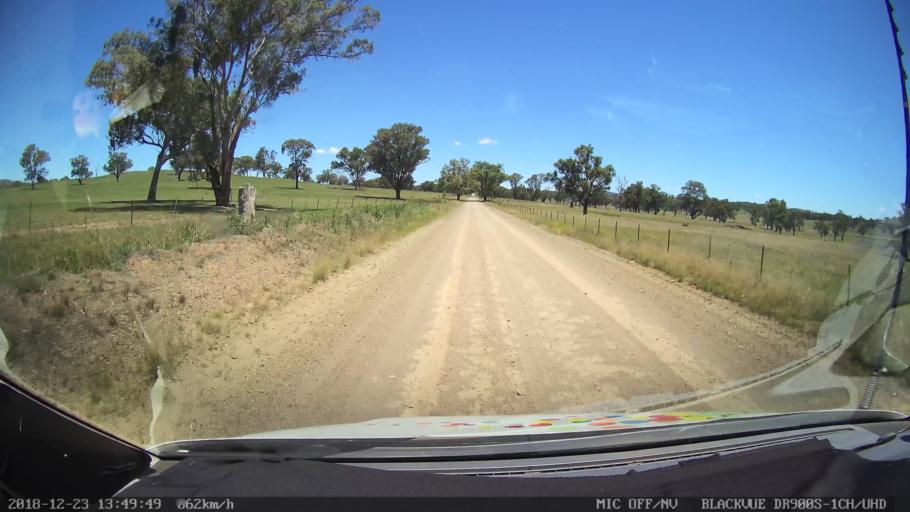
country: AU
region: New South Wales
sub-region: Tamworth Municipality
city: Manilla
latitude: -30.5248
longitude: 151.1078
